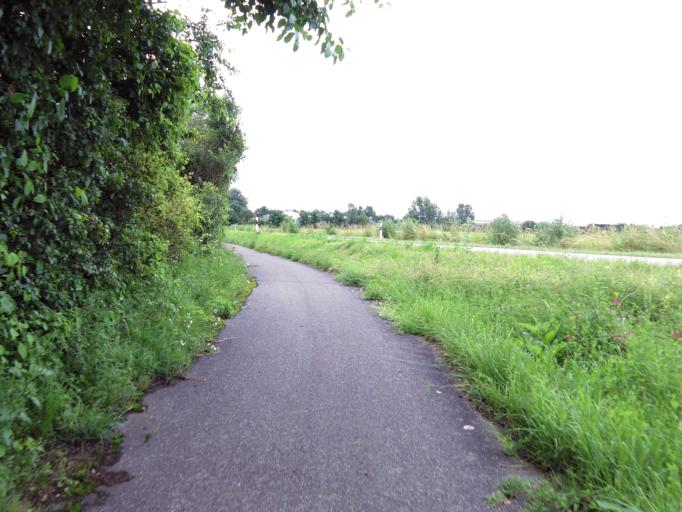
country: DE
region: Rheinland-Pfalz
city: Hessheim
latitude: 49.5583
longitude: 8.3066
